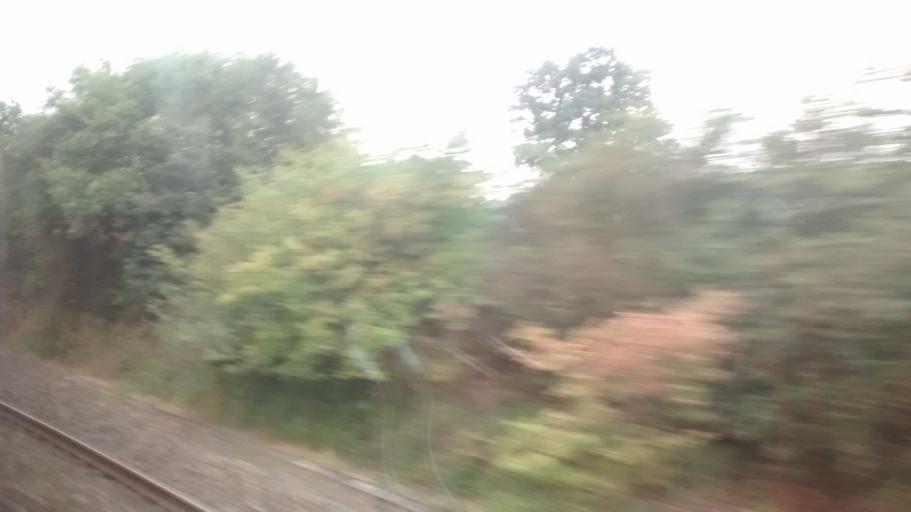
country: FR
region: Pays de la Loire
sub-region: Departement de la Mayenne
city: Sainte-Suzanne
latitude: 48.1459
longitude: -0.2506
